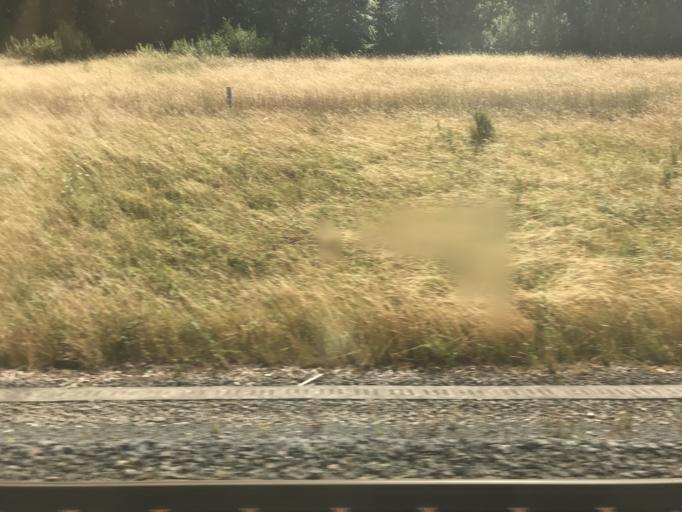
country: FR
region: Lorraine
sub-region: Departement de la Moselle
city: Solgne
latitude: 48.9633
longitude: 6.3371
